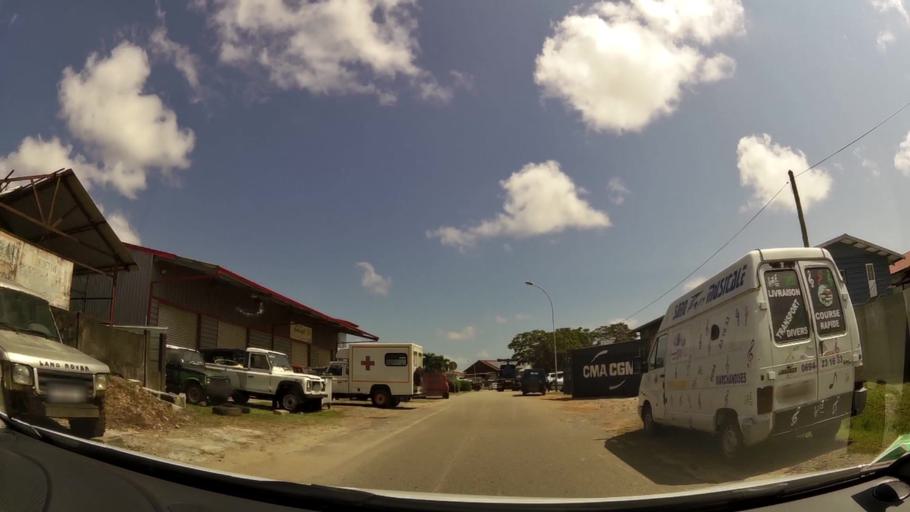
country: GF
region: Guyane
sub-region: Guyane
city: Cayenne
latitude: 4.9301
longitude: -52.3272
